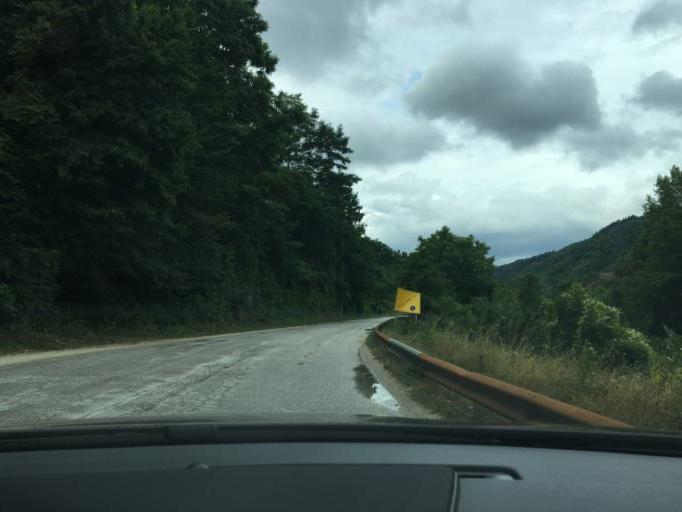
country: MK
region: Kriva Palanka
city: Kriva Palanka
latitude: 42.2233
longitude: 22.3949
